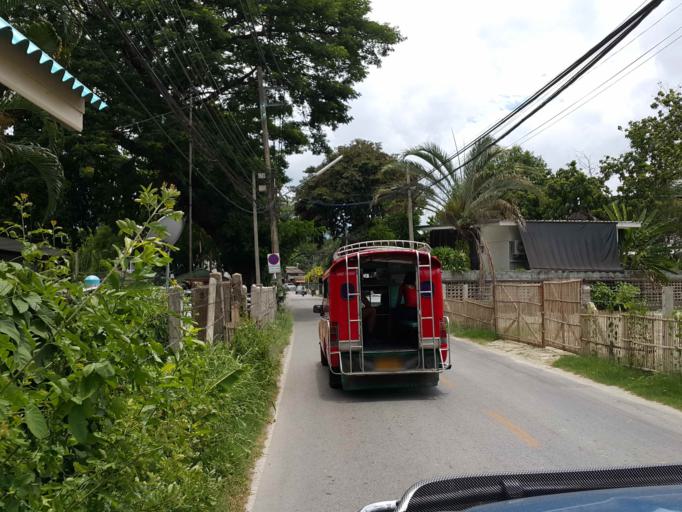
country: TH
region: Chiang Mai
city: Chiang Mai
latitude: 18.7749
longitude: 99.0095
